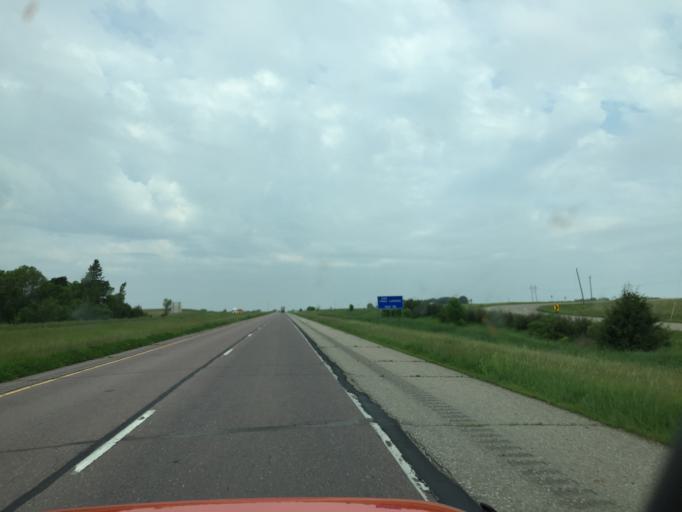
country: US
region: Minnesota
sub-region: Martin County
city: Fairmont
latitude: 43.6793
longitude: -94.4745
